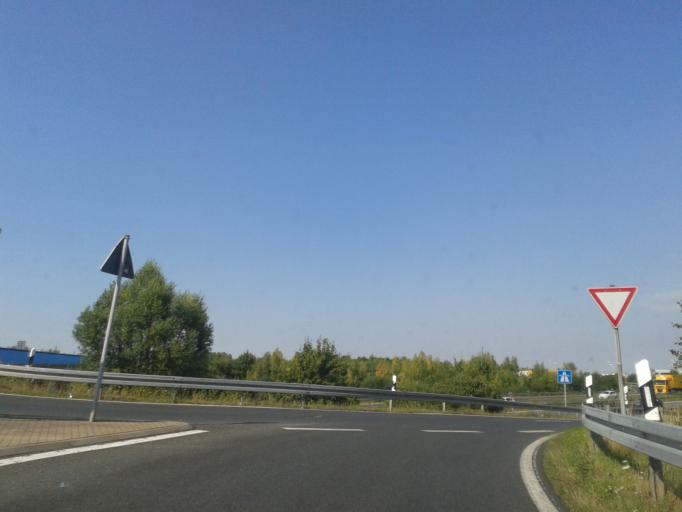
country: DE
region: Saxony
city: Nossen
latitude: 51.0342
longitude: 13.2937
